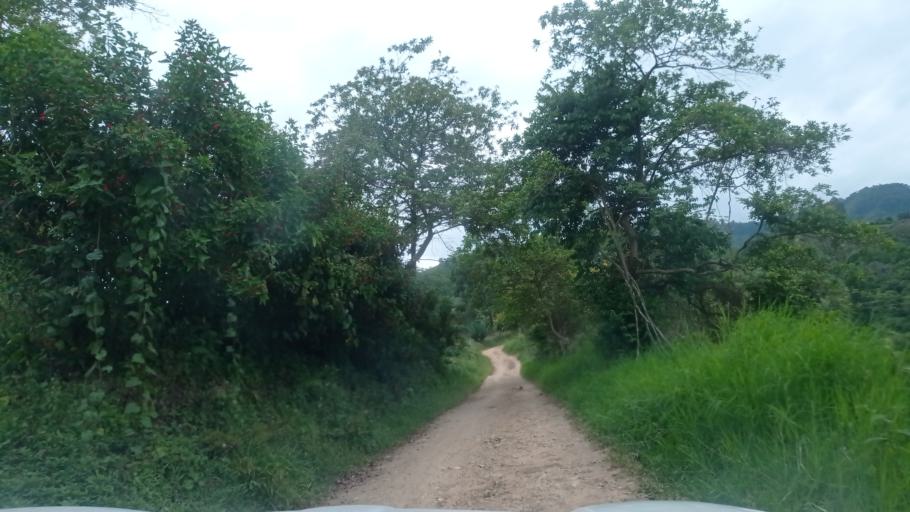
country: CO
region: Huila
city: Garzon
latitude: 2.0986
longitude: -75.6281
